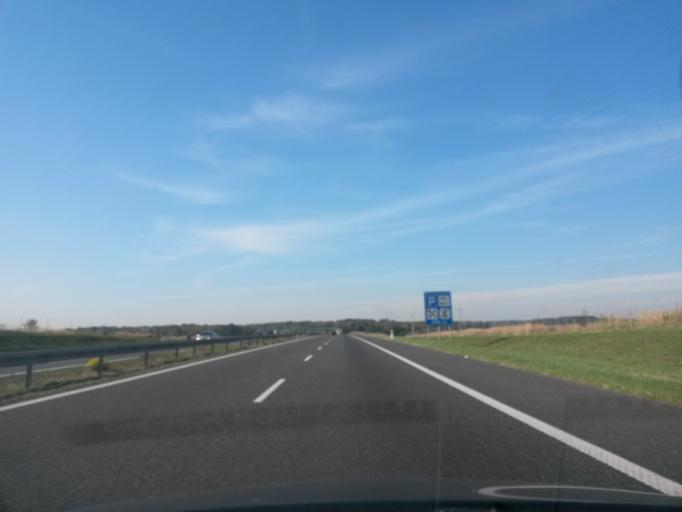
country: PL
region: Opole Voivodeship
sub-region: Powiat strzelecki
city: Ujazd
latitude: 50.4178
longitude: 18.4018
